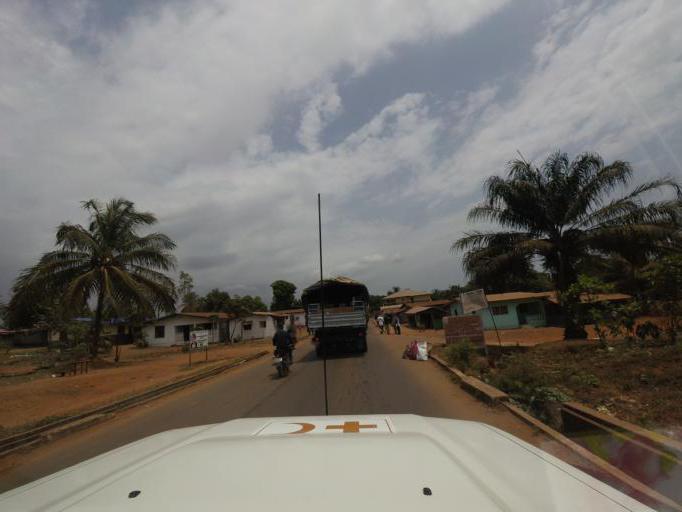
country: LR
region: Montserrado
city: Monrovia
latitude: 6.3072
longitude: -10.6957
